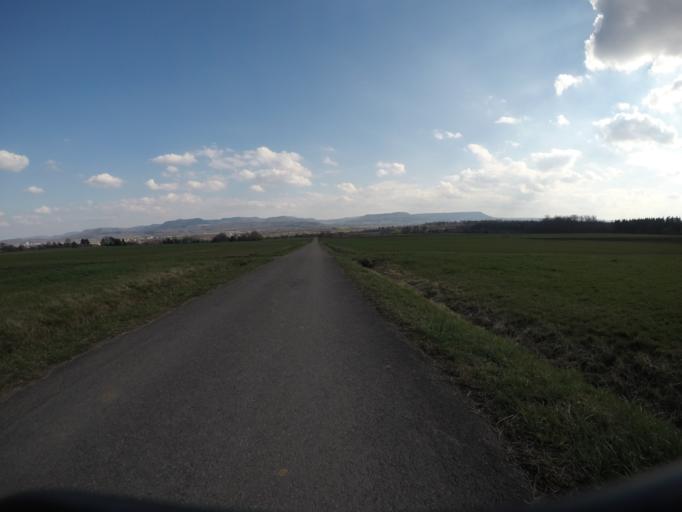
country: DE
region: Baden-Wuerttemberg
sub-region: Tuebingen Region
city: Dusslingen
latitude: 48.4548
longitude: 9.0275
